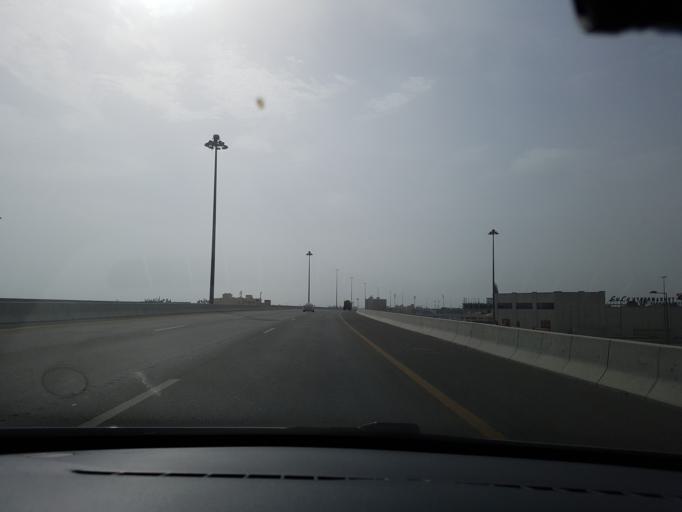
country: OM
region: Al Batinah
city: Al Sohar
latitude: 24.3423
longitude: 56.7286
